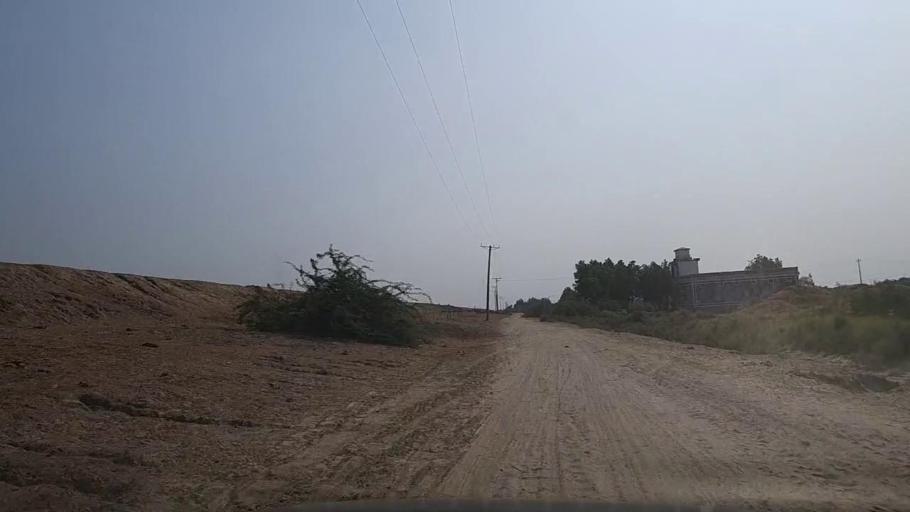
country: PK
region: Sindh
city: Chuhar Jamali
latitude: 24.5582
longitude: 67.9153
